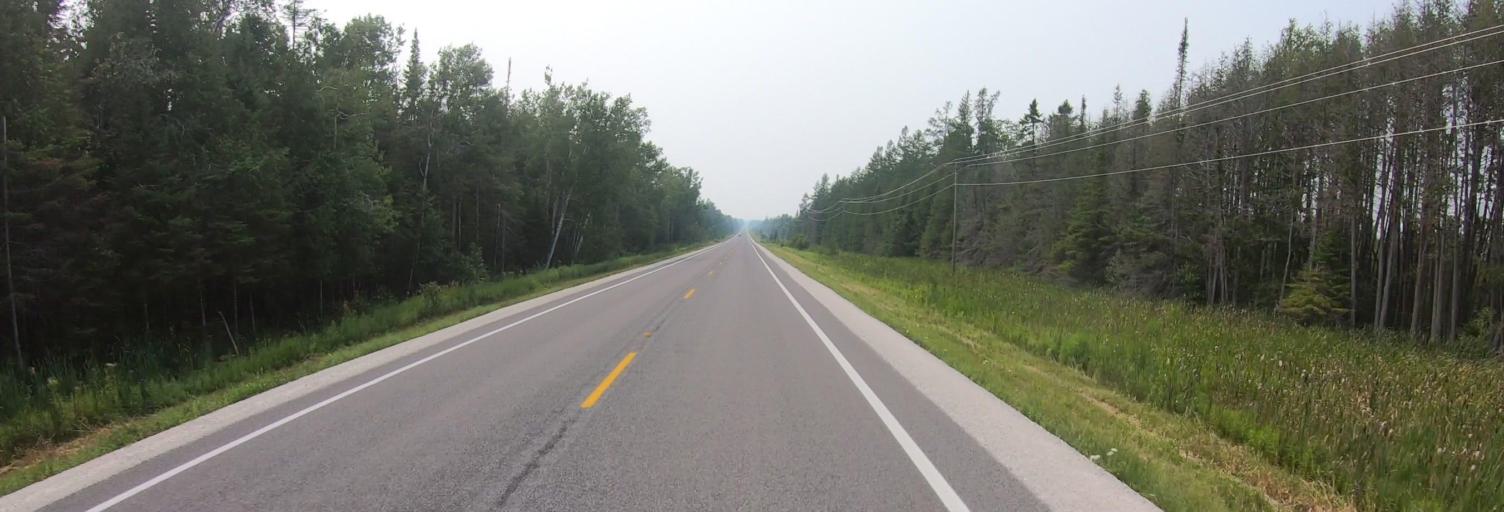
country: US
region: Michigan
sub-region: Chippewa County
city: Sault Ste. Marie
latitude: 46.0720
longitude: -84.1849
